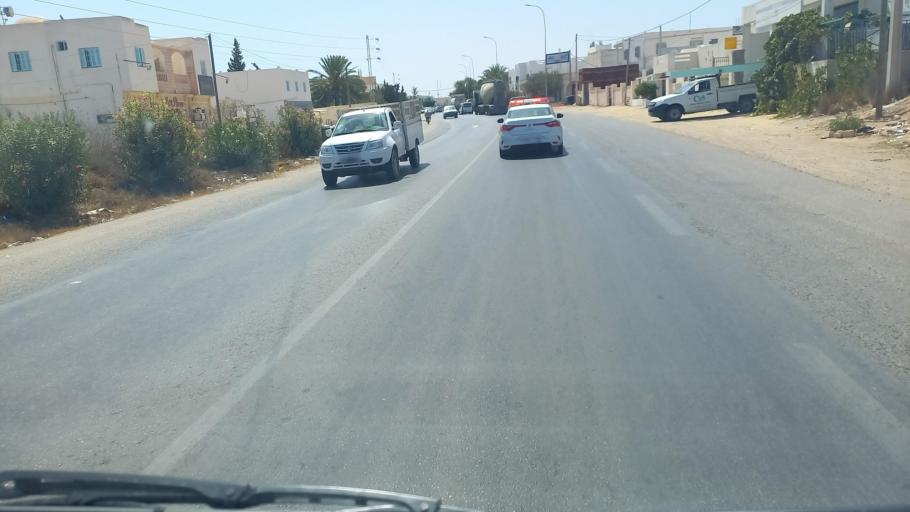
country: TN
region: Madanin
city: Houmt Souk
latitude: 33.8056
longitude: 10.8816
